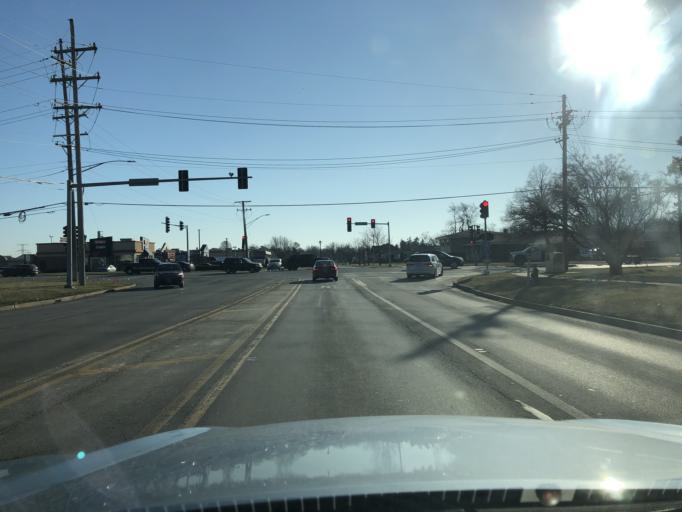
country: US
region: Illinois
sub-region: DuPage County
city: Itasca
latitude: 41.9672
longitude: -87.9984
